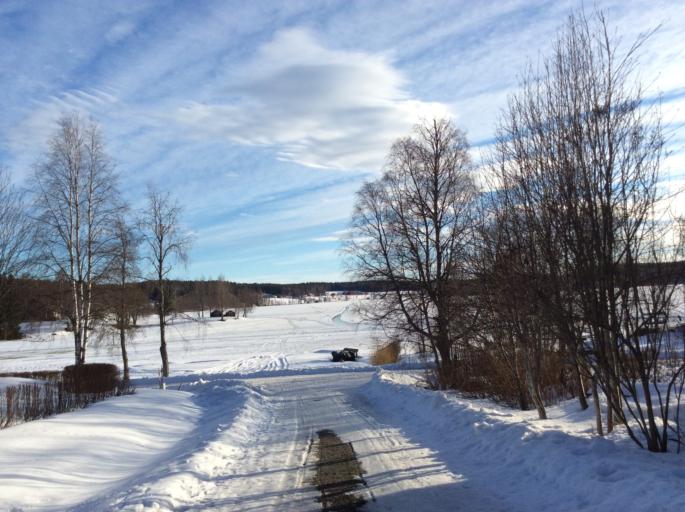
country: SE
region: Vaesterbotten
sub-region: Umea Kommun
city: Roback
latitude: 64.0381
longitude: 20.0736
